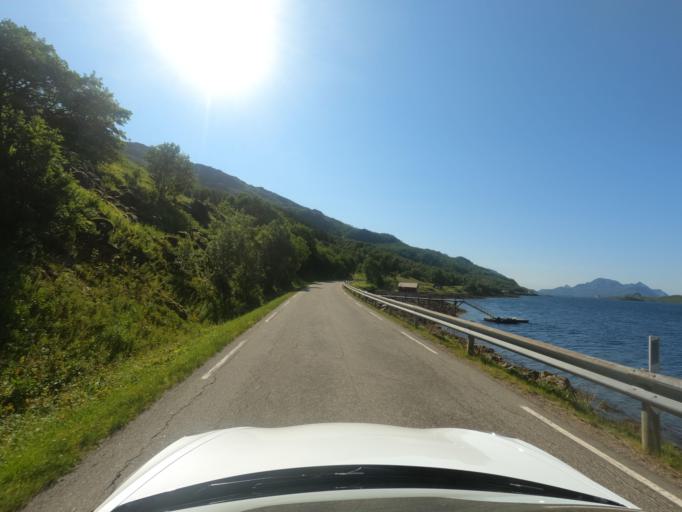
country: NO
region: Nordland
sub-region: Hadsel
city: Stokmarknes
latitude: 68.3833
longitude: 15.0898
